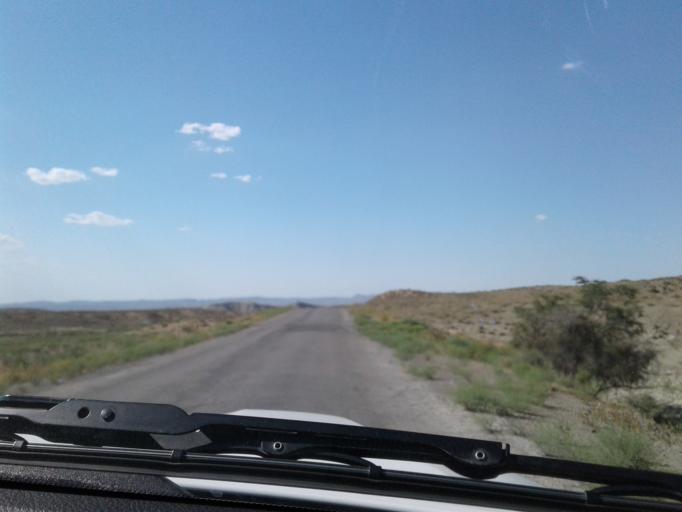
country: TM
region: Balkan
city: Magtymguly
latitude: 38.5103
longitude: 56.1909
